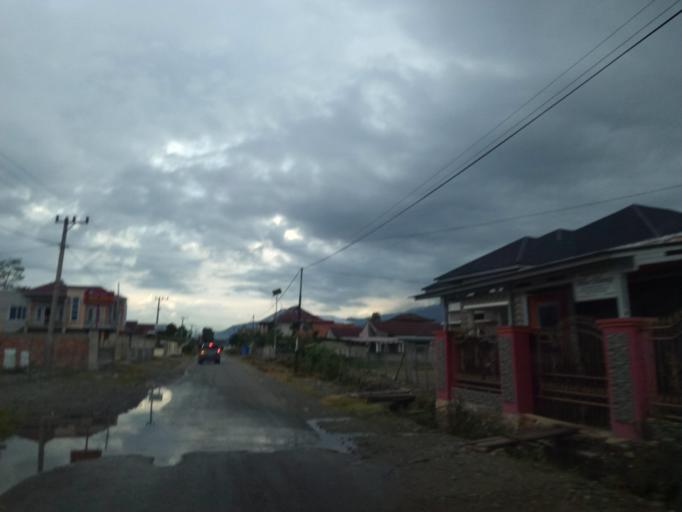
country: ID
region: Jambi
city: Semurup
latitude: -1.9875
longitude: 101.3585
